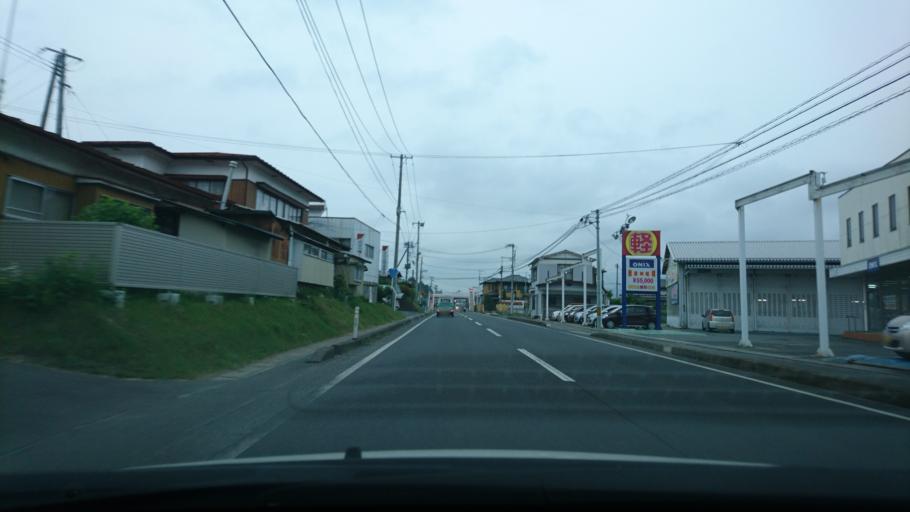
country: JP
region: Iwate
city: Ichinoseki
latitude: 38.9140
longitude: 141.1315
